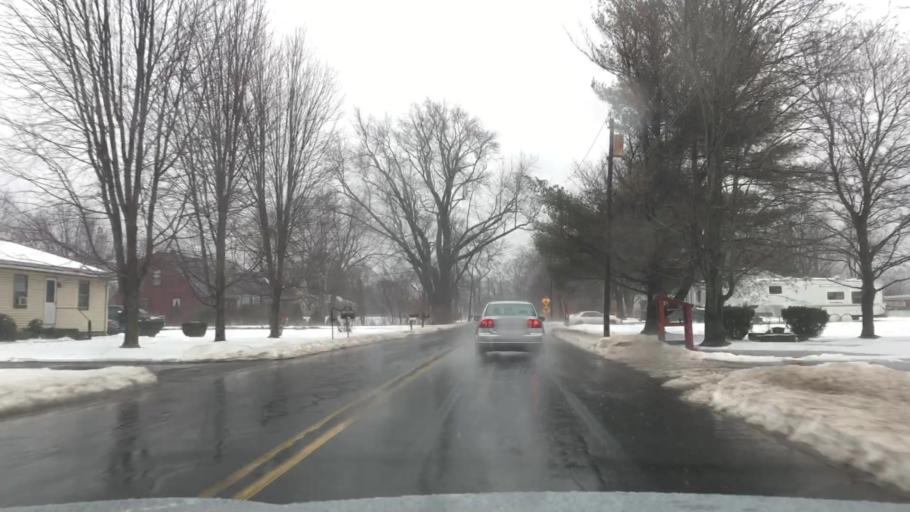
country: US
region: Massachusetts
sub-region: Hampshire County
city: Granby
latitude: 42.2238
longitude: -72.4972
